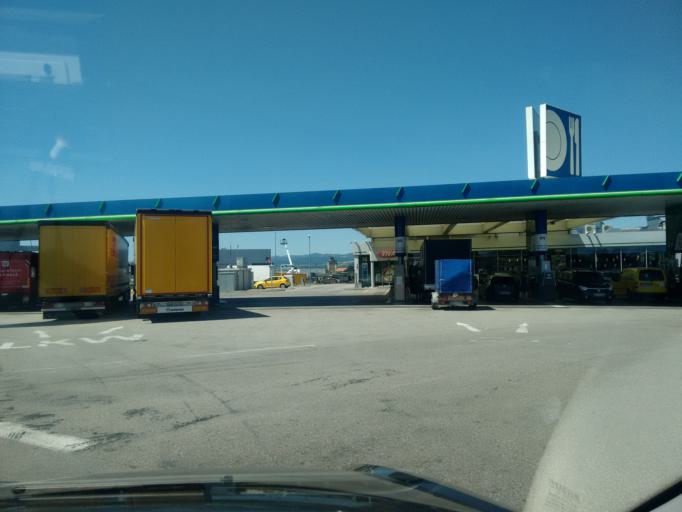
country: AT
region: Lower Austria
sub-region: Politischer Bezirk Melk
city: Loosdorf
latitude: 48.1895
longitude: 15.4091
